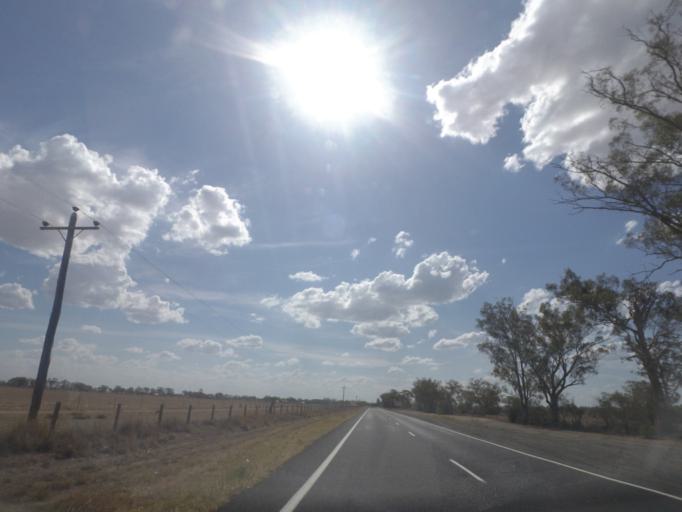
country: AU
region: New South Wales
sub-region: Moree Plains
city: Boggabilla
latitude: -28.4118
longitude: 151.1046
